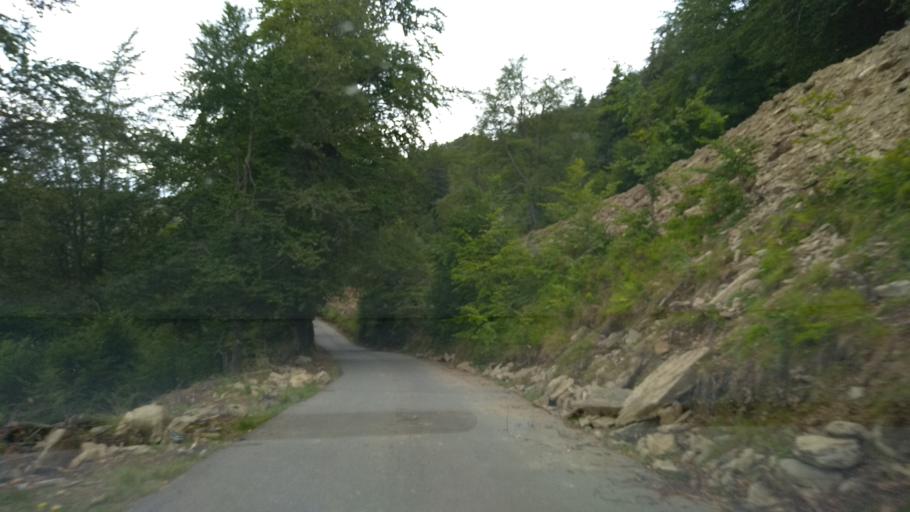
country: RO
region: Hunedoara
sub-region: Municipiul  Vulcan
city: Jiu-Paroseni
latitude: 45.3246
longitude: 23.2917
